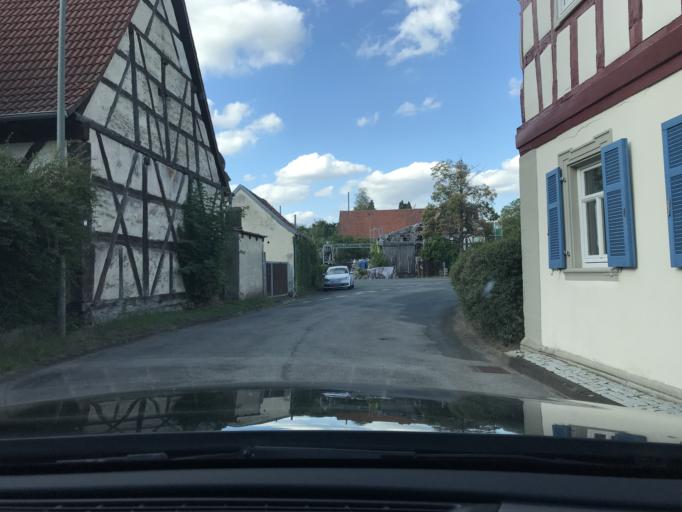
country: DE
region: Bavaria
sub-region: Regierungsbezirk Unterfranken
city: Kirchlauter
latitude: 50.0614
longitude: 10.6724
